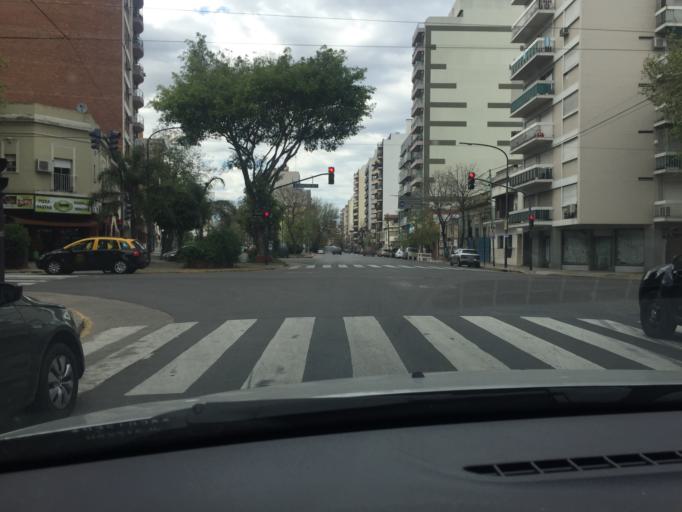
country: AR
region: Buenos Aires
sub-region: Partido de General San Martin
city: General San Martin
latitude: -34.5702
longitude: -58.4915
